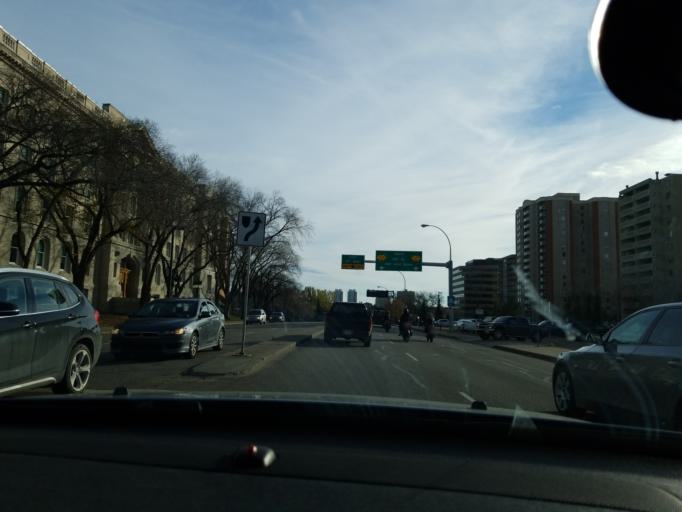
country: CA
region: Alberta
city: Edmonton
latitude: 53.5372
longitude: -113.5085
